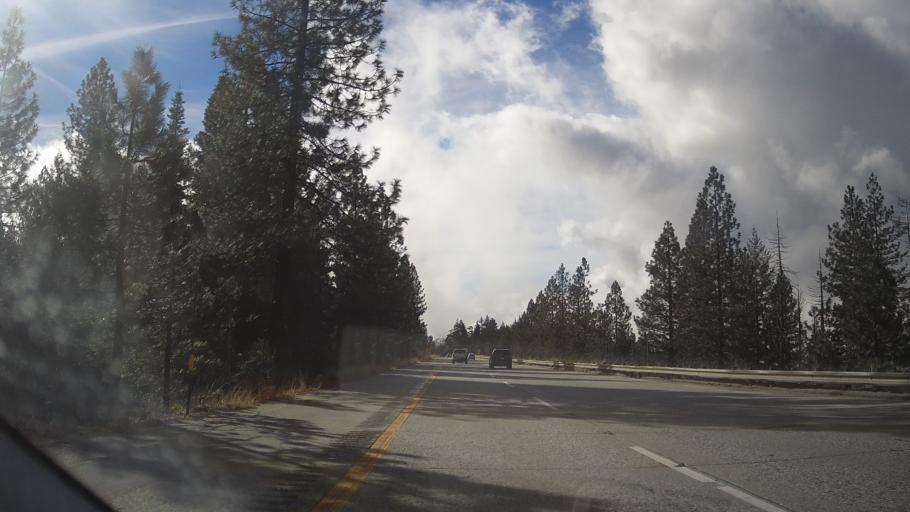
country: US
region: California
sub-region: Placer County
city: Foresthill
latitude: 39.2829
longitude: -120.7070
